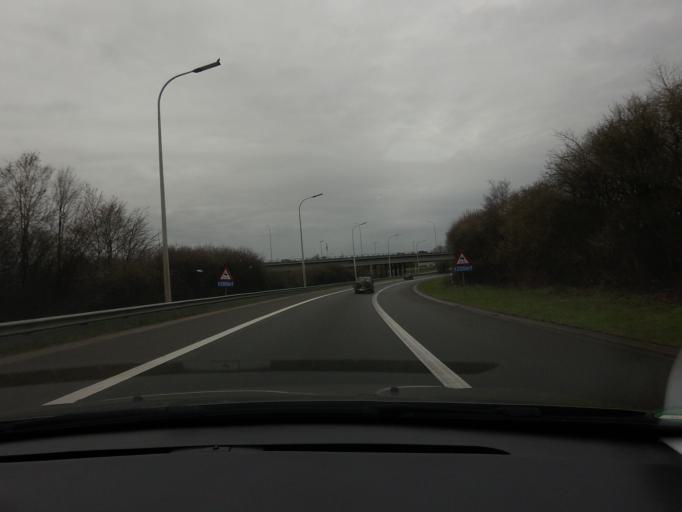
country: BE
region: Wallonia
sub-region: Province de Liege
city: Ans
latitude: 50.6681
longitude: 5.4955
